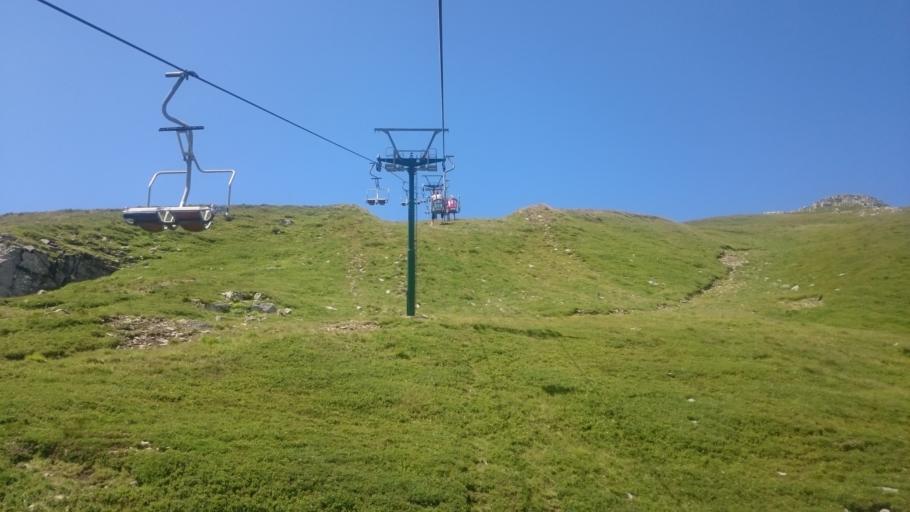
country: IT
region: Emilia-Romagna
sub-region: Provincia di Reggio Emilia
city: Ligonchio
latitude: 44.2837
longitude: 10.4040
